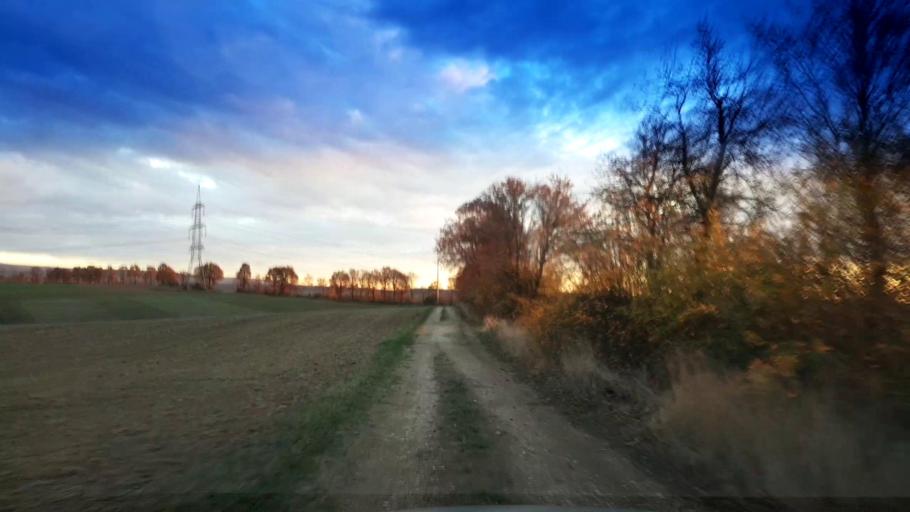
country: DE
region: Bavaria
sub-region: Upper Franconia
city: Memmelsdorf
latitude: 49.9622
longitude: 10.9766
